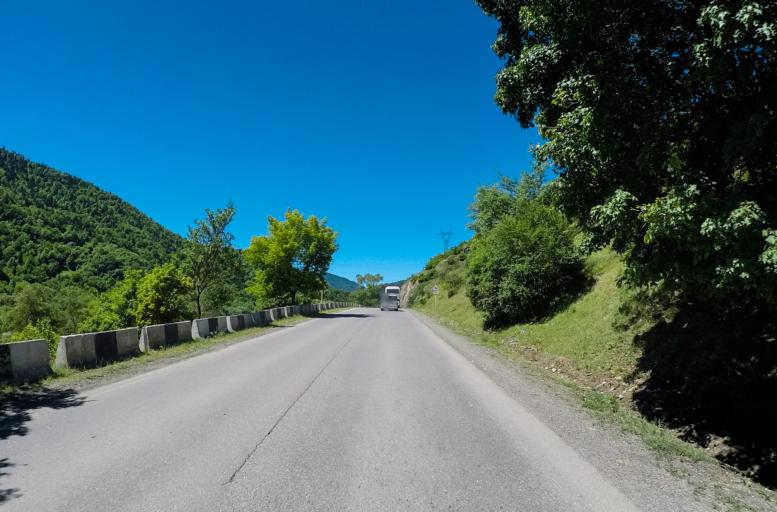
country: GE
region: Samtskhe-Javakheti
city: Borjomi
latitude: 41.8013
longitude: 43.3172
